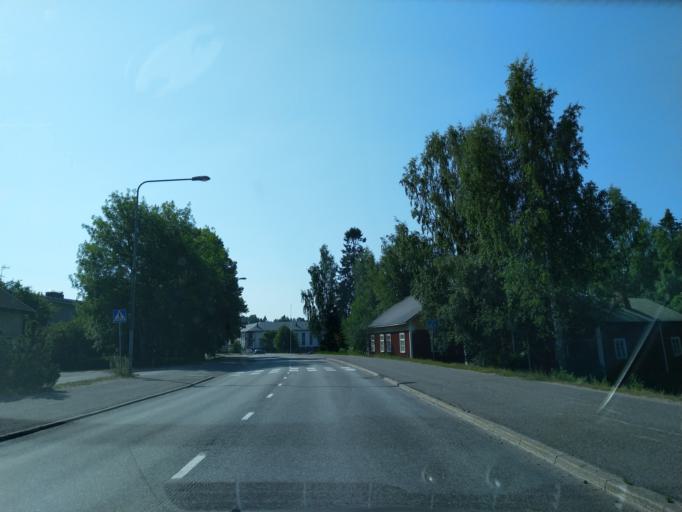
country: FI
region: Satakunta
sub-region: Pori
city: Noormarkku
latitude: 61.5941
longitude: 21.8671
